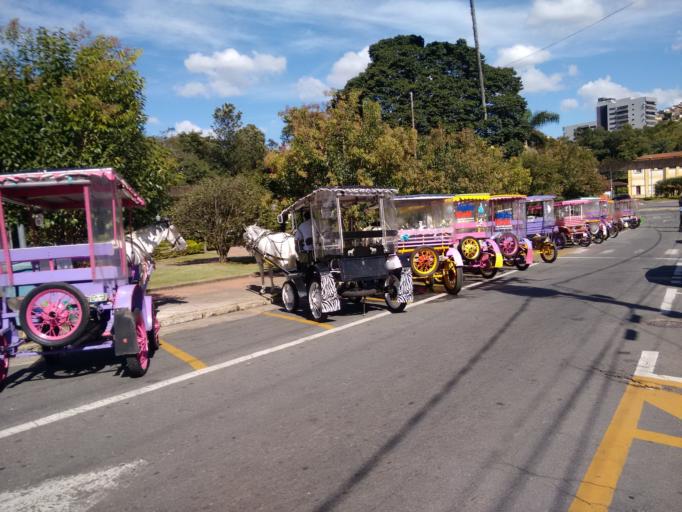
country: BR
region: Minas Gerais
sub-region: Pocos De Caldas
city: Pocos de Caldas
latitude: -21.7854
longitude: -46.5712
